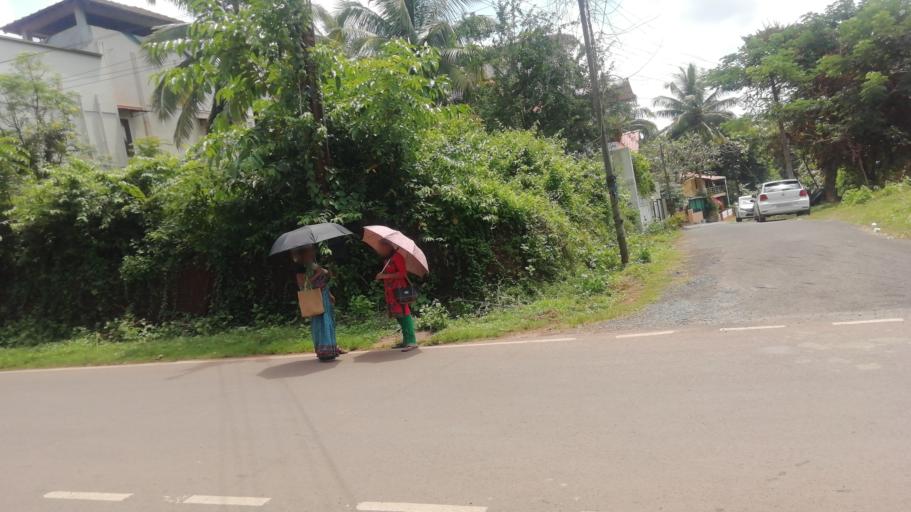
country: IN
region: Goa
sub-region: North Goa
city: Queula
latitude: 15.3854
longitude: 74.0015
